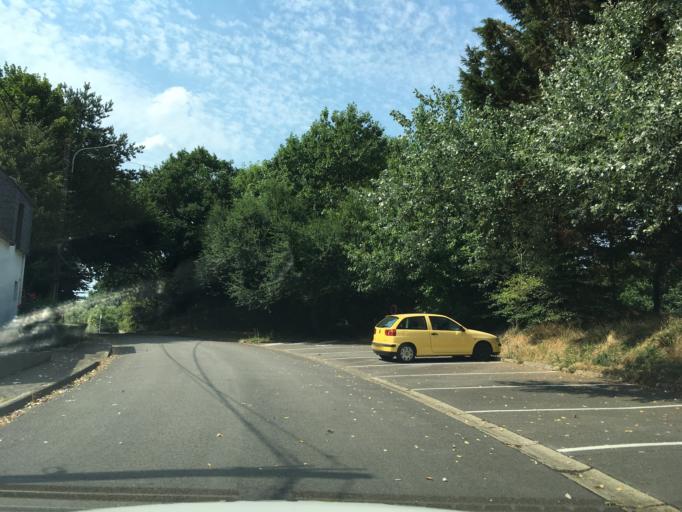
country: FR
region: Brittany
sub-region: Departement du Morbihan
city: Lorient
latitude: 47.7695
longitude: -3.3830
